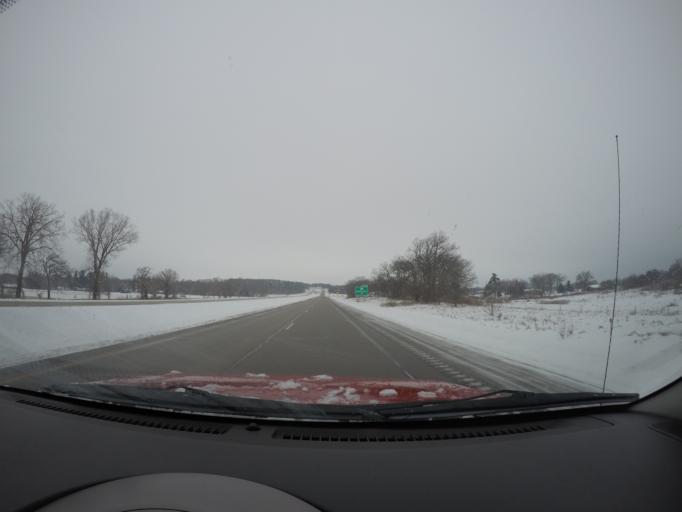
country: US
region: Minnesota
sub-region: Olmsted County
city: Eyota
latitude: 43.9534
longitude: -92.3500
